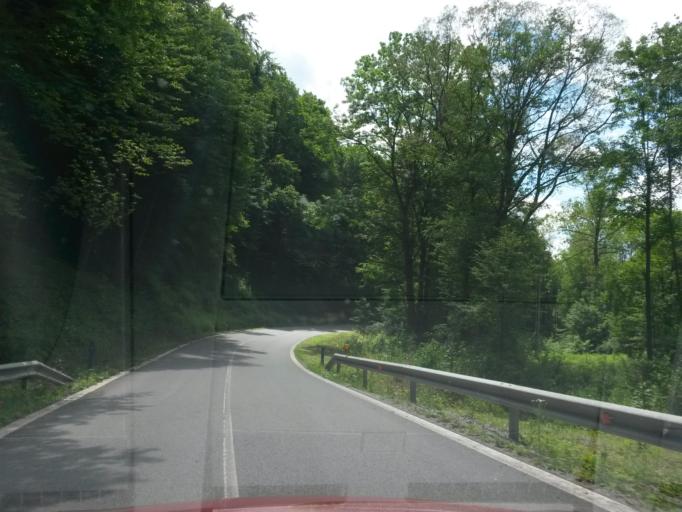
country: SK
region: Kosicky
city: Gelnica
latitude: 48.9074
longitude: 21.0280
